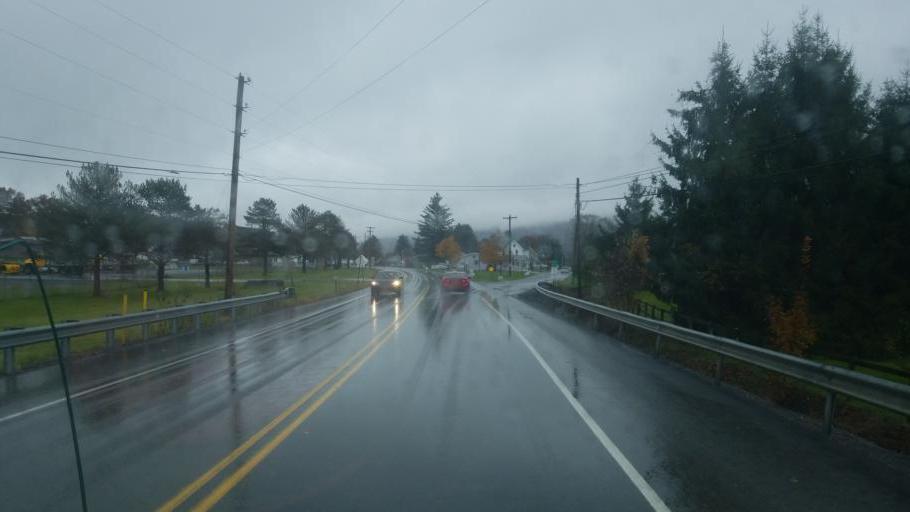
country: US
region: Pennsylvania
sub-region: Clinton County
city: Mill Hall
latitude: 41.1123
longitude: -77.5002
